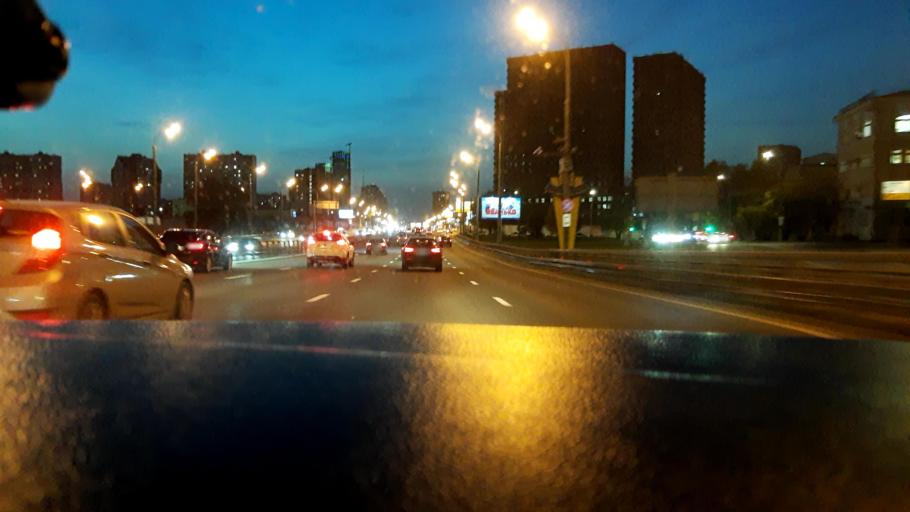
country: RU
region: Moscow
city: Sokol
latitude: 55.7713
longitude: 37.5033
